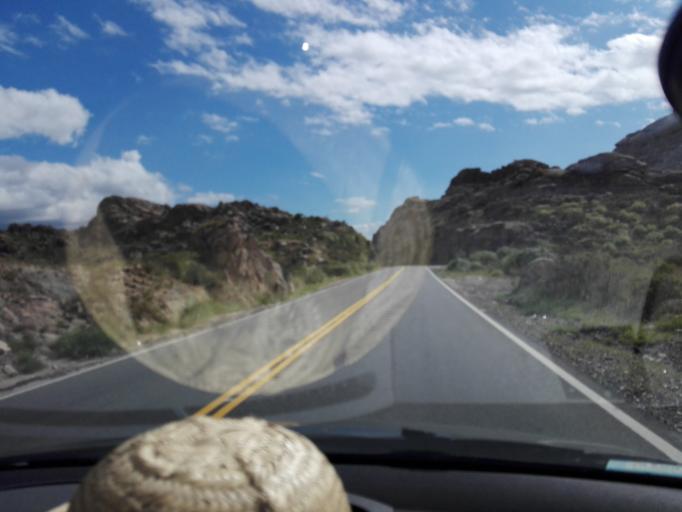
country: AR
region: Cordoba
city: Mina Clavero
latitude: -31.7604
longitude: -64.9136
